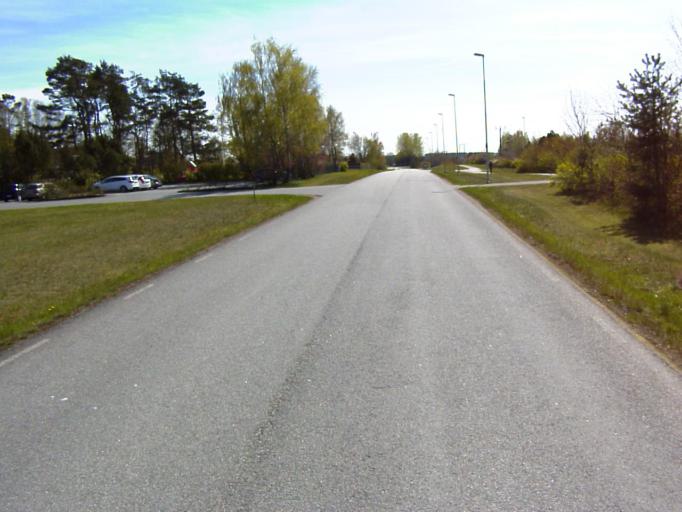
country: SE
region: Skane
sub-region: Kristianstads Kommun
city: Norra Asum
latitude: 55.9981
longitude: 14.0788
